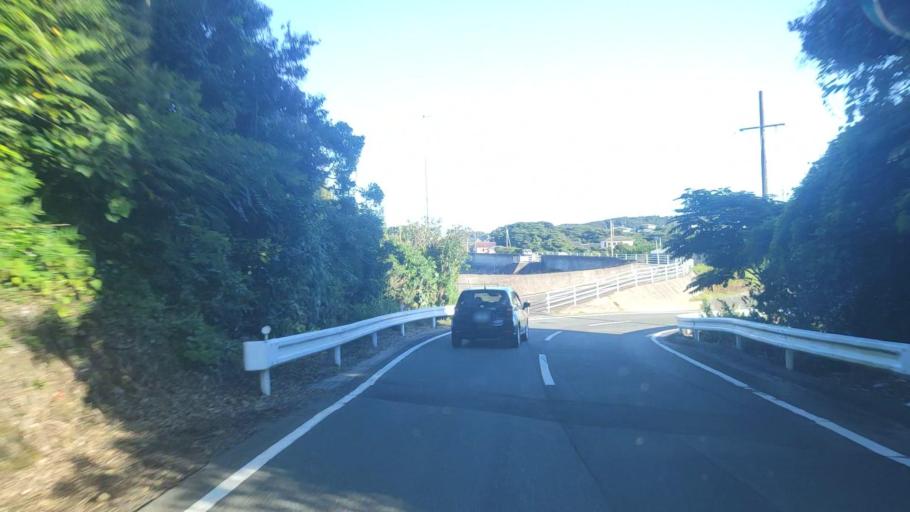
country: JP
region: Mie
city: Toba
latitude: 34.3208
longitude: 136.8826
